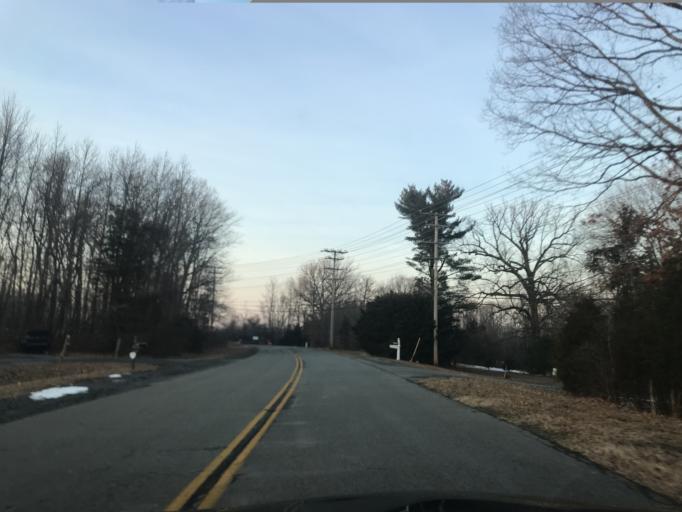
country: US
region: Maryland
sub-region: Harford County
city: Edgewood
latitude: 39.4562
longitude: -76.3060
